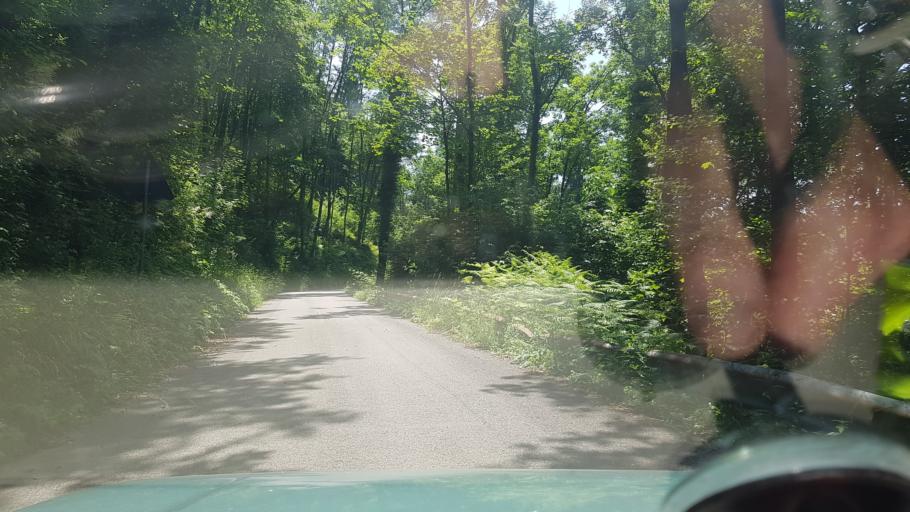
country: IT
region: Friuli Venezia Giulia
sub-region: Provincia di Udine
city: Lusevera
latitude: 46.2620
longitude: 13.2897
